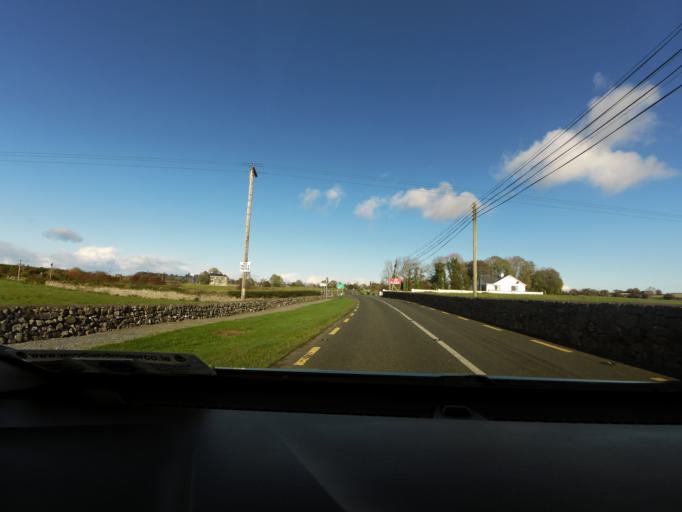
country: IE
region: Connaught
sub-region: Maigh Eo
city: Ballinrobe
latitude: 53.5745
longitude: -9.1218
